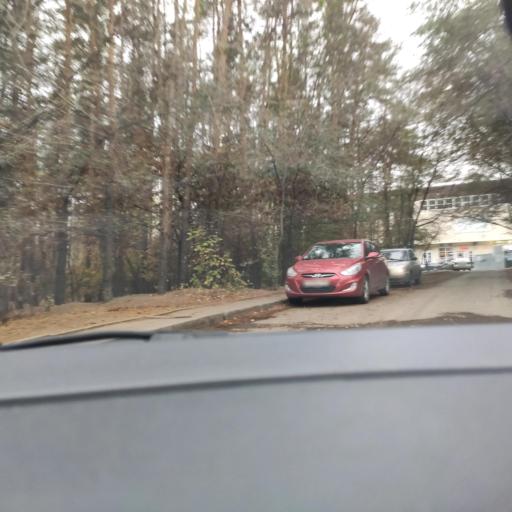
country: RU
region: Voronezj
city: Podgornoye
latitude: 51.6853
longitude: 39.1300
